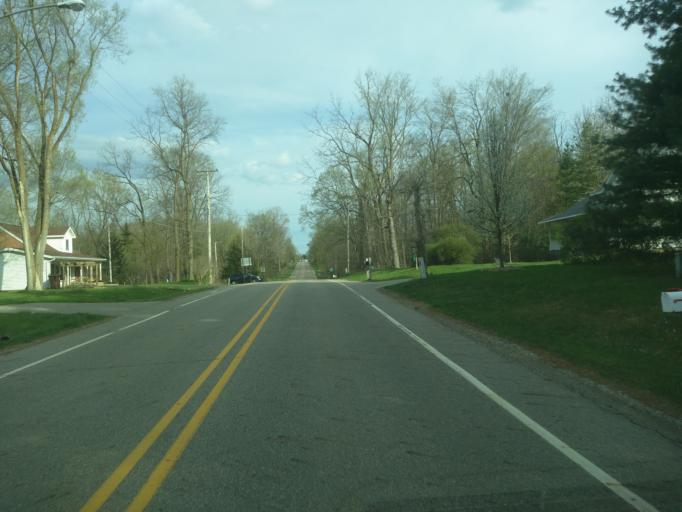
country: US
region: Michigan
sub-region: Eaton County
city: Dimondale
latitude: 42.6396
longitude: -84.6483
